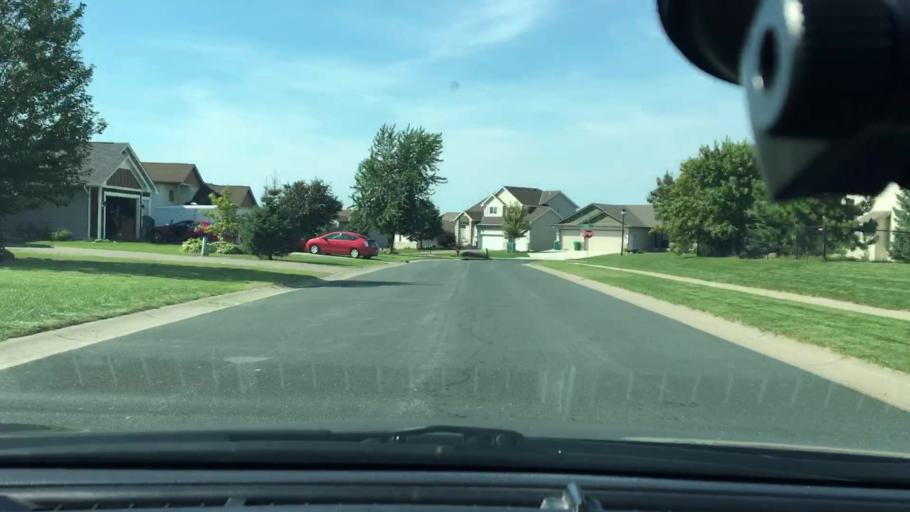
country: US
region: Minnesota
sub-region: Wright County
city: Albertville
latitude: 45.2577
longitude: -93.6566
